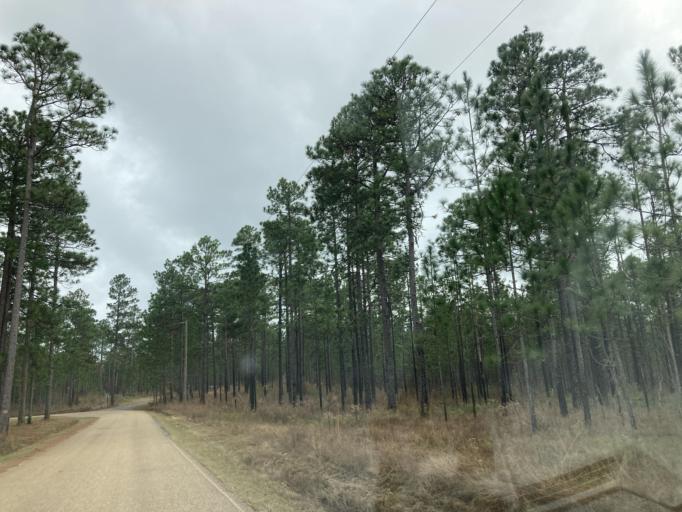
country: US
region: Mississippi
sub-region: Lamar County
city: Lumberton
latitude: 31.0976
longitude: -89.5345
